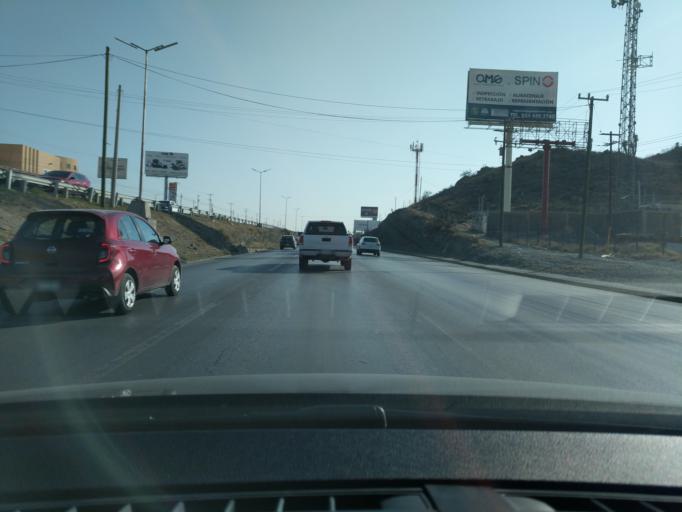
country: MX
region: Coahuila
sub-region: Ramos Arizpe
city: Ramos Arizpe
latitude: 25.5145
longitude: -100.9586
